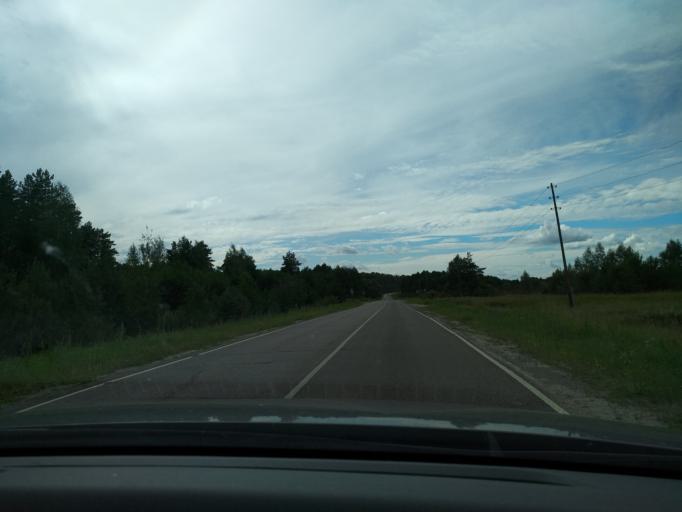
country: RU
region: Moskovskaya
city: Krasnyy Tkach
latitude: 55.3804
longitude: 39.2012
